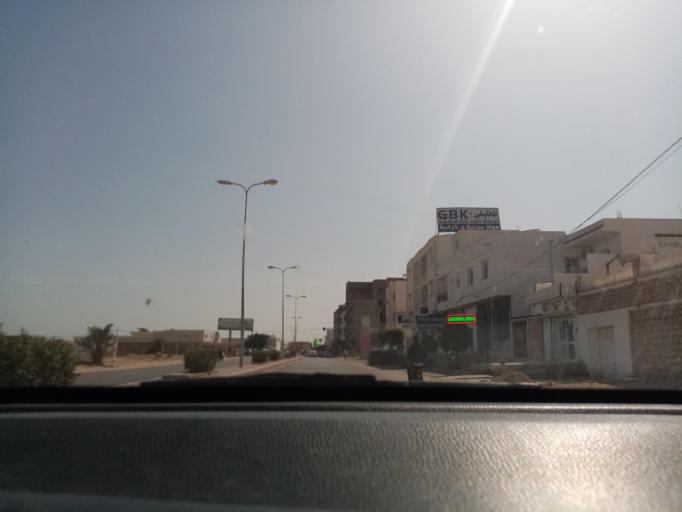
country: TN
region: Qabis
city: Gabes
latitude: 33.8511
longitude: 10.1099
